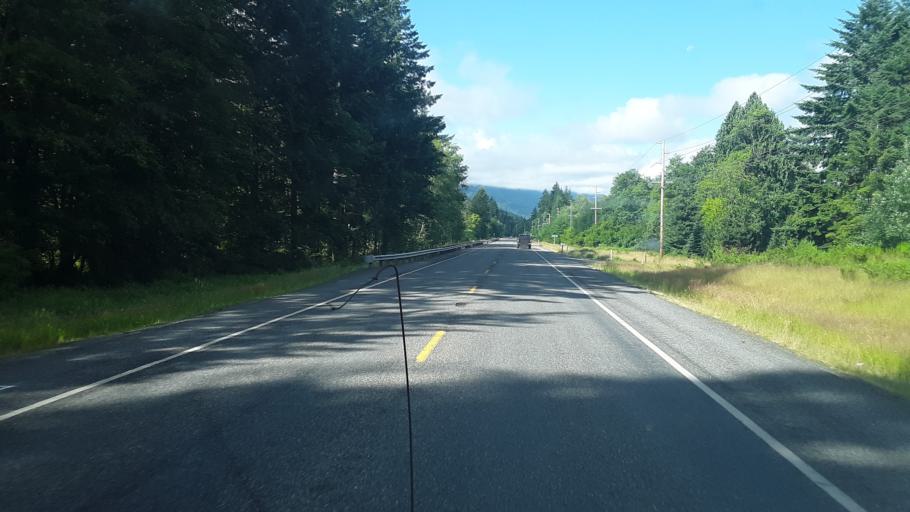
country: US
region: Washington
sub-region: Lewis County
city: Morton
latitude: 46.5512
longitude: -121.7380
